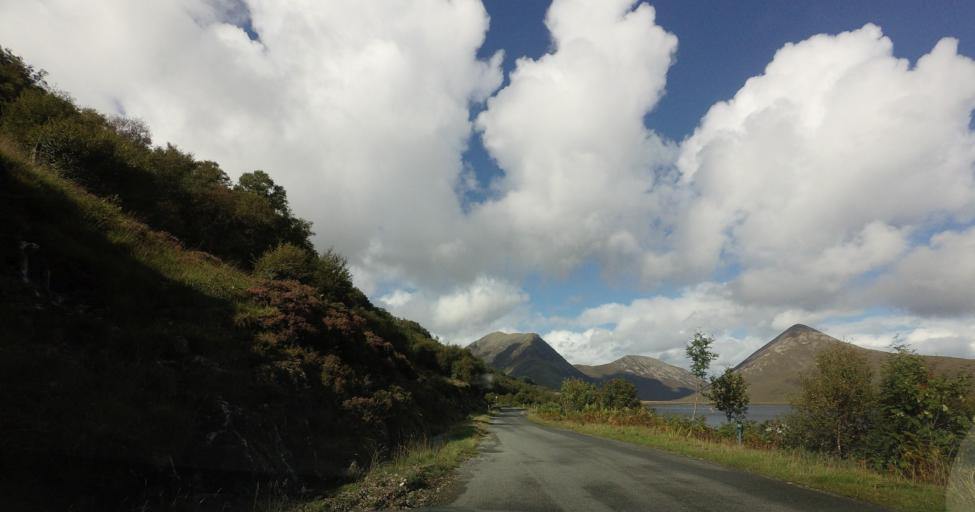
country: GB
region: Scotland
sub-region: Highland
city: Portree
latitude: 57.2101
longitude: -6.0329
